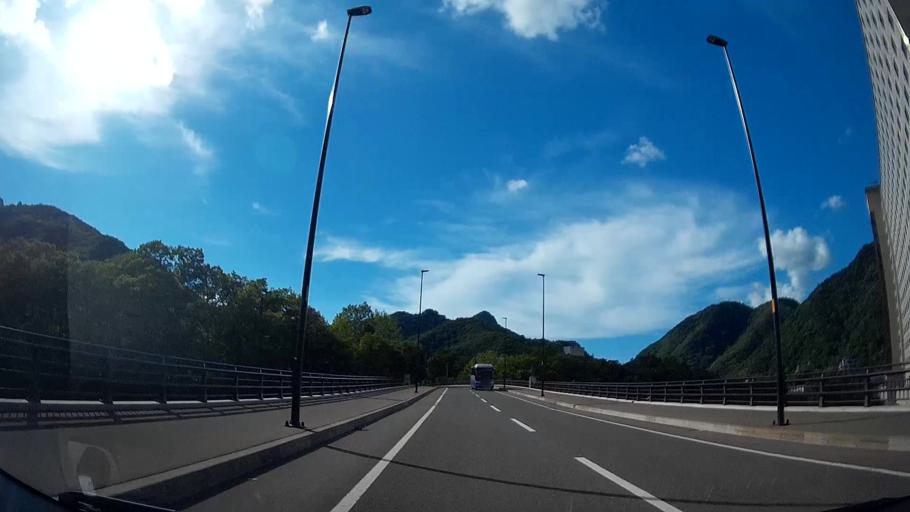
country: JP
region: Hokkaido
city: Sapporo
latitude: 42.9684
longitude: 141.1668
